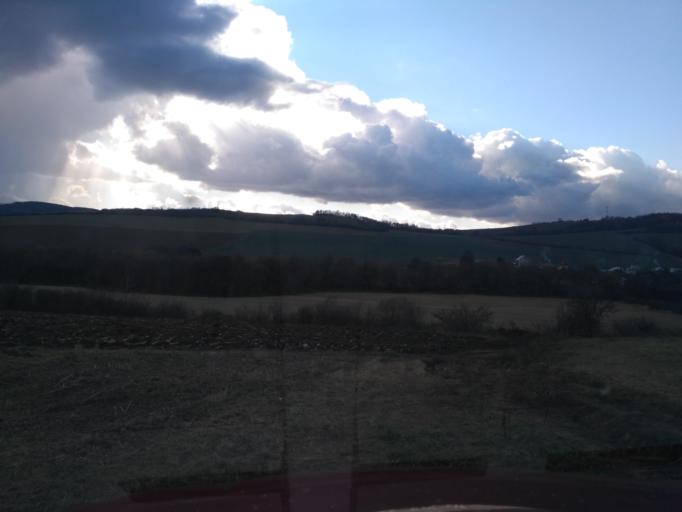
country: SK
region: Presovsky
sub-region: Okres Presov
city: Presov
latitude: 48.9257
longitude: 21.1980
